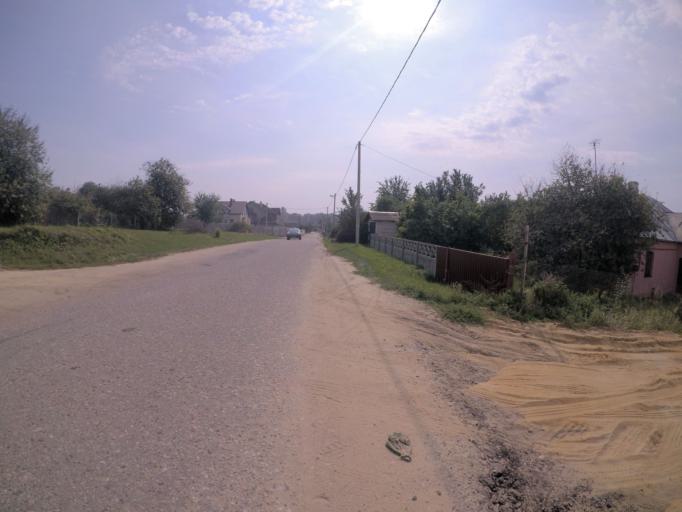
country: BY
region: Grodnenskaya
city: Hrodna
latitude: 53.7215
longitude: 23.8473
